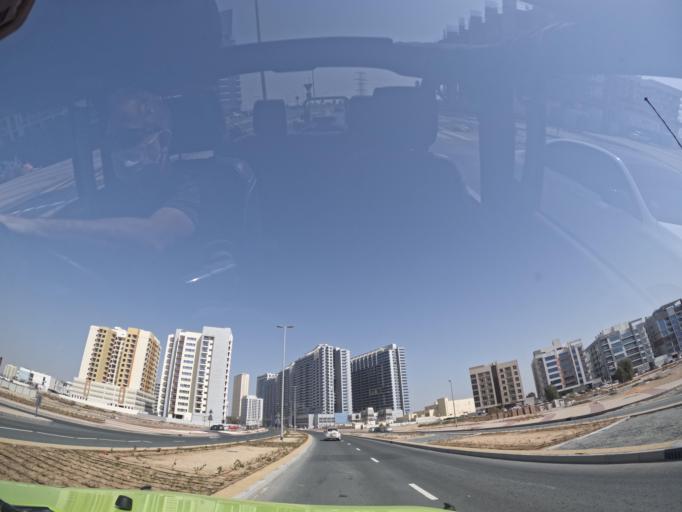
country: AE
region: Dubai
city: Dubai
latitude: 25.0869
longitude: 55.3860
